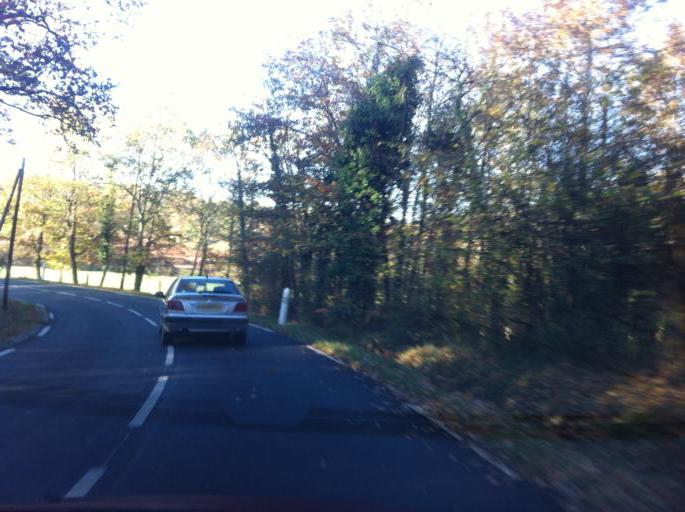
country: FR
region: Aquitaine
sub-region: Departement de la Dordogne
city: Riberac
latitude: 45.2740
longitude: 0.2536
